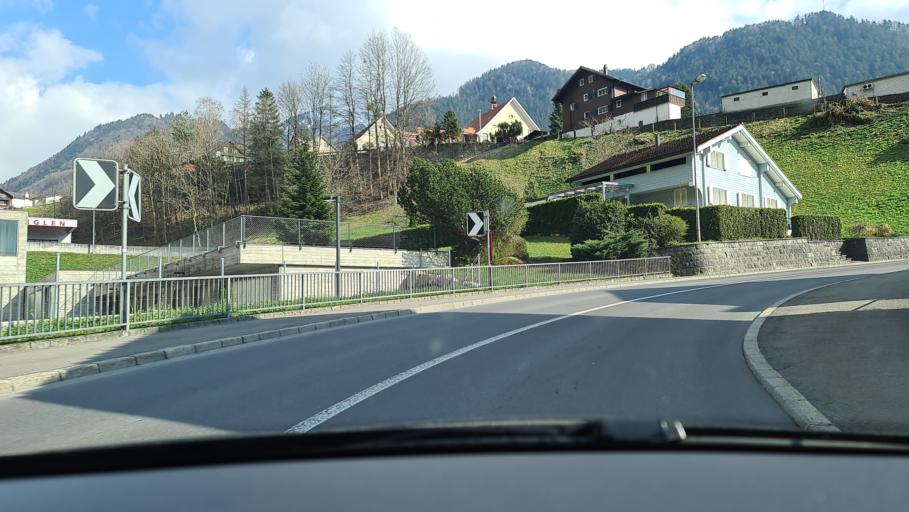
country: CH
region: Uri
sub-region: Uri
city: Burglen
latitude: 46.8769
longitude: 8.6632
